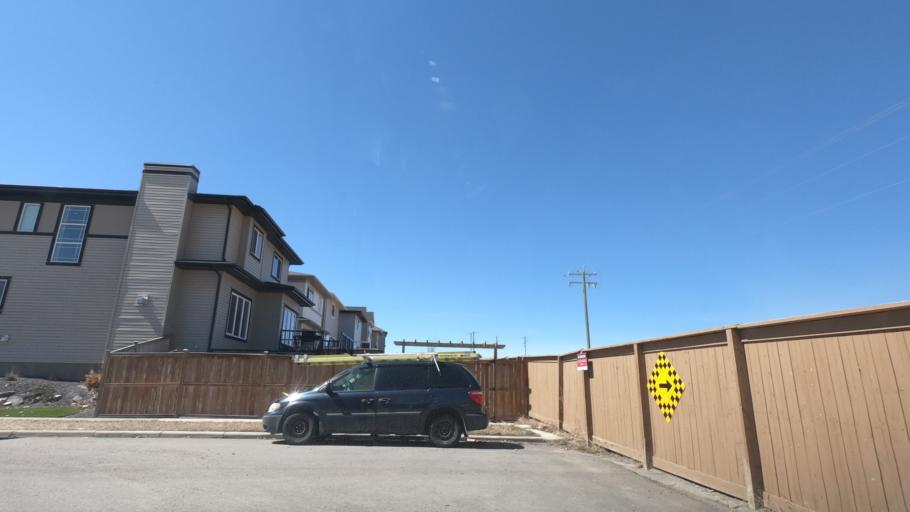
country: CA
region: Alberta
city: Airdrie
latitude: 51.3074
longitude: -114.0463
